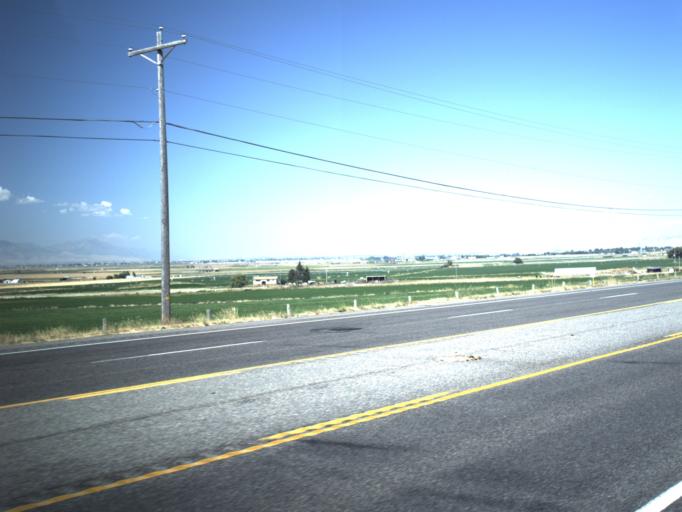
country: US
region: Utah
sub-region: Cache County
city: Smithfield
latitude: 41.8757
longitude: -111.8242
